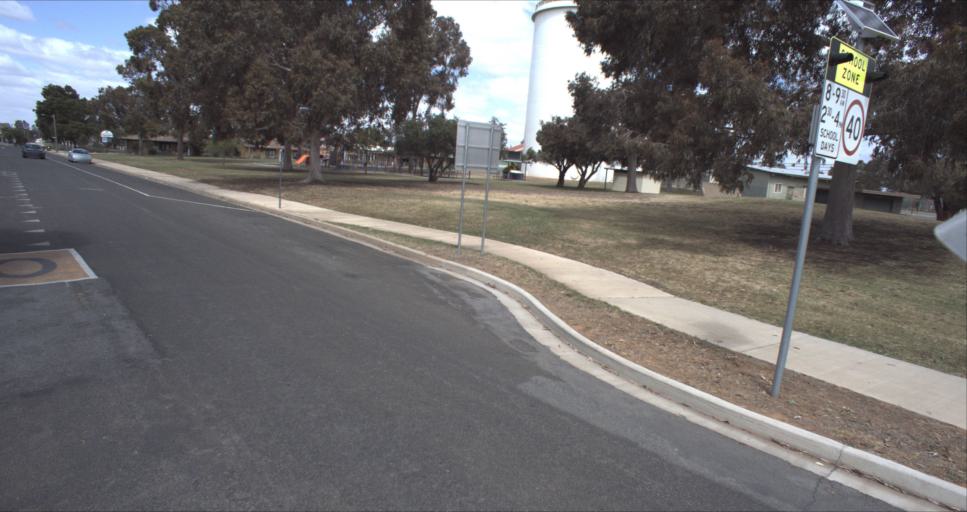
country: AU
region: New South Wales
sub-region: Leeton
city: Leeton
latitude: -34.5608
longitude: 146.3973
